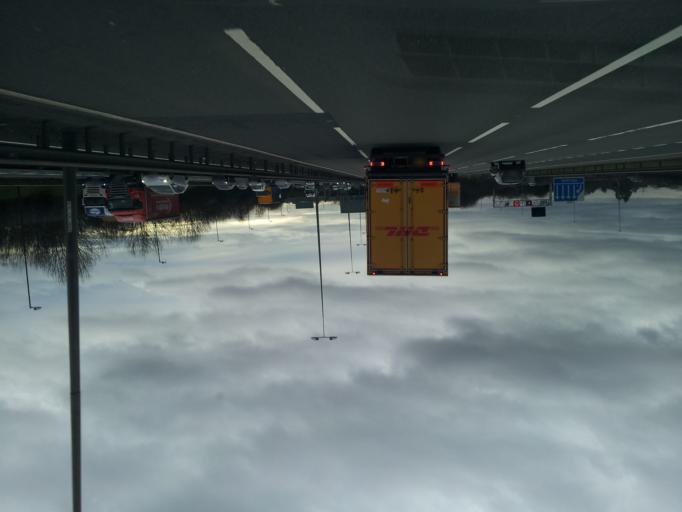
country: GB
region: England
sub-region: Warwickshire
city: Water Orton
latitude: 52.5147
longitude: -1.7252
